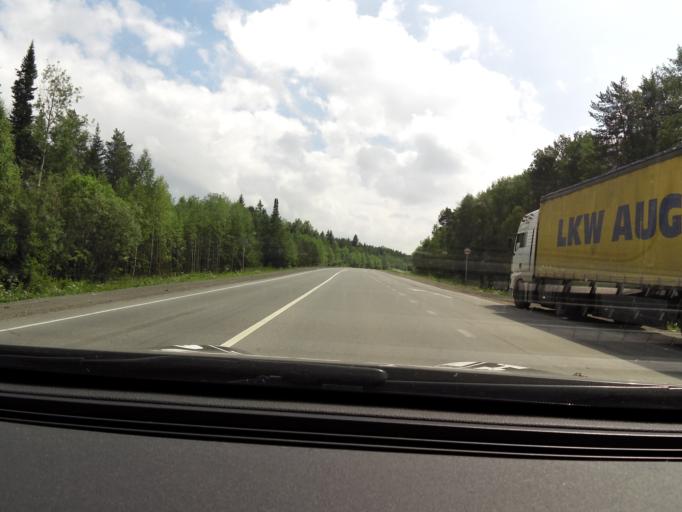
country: RU
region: Perm
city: Suksun
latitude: 57.0127
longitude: 57.4711
